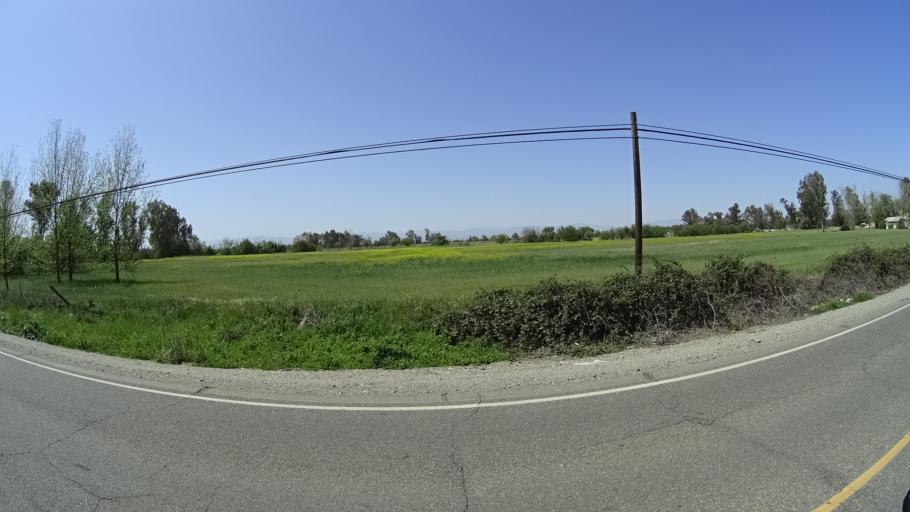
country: US
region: California
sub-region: Glenn County
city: Orland
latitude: 39.7054
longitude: -122.1968
